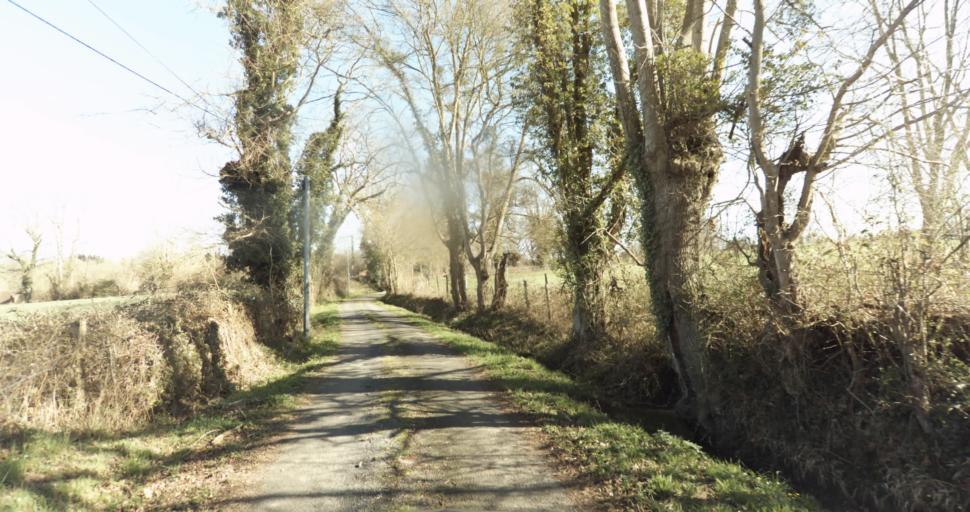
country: FR
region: Lower Normandy
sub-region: Departement du Calvados
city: Livarot
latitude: 49.0265
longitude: 0.0657
